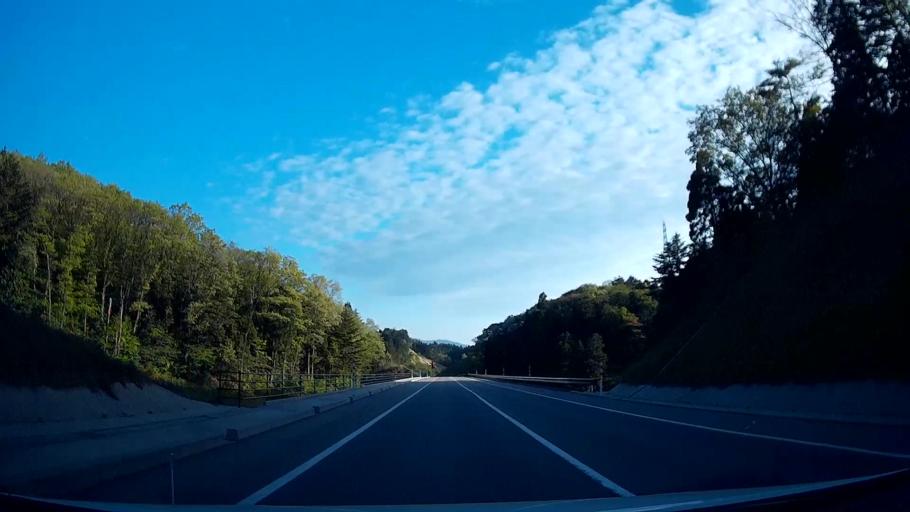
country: JP
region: Ishikawa
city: Nanao
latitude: 37.0398
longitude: 136.9482
